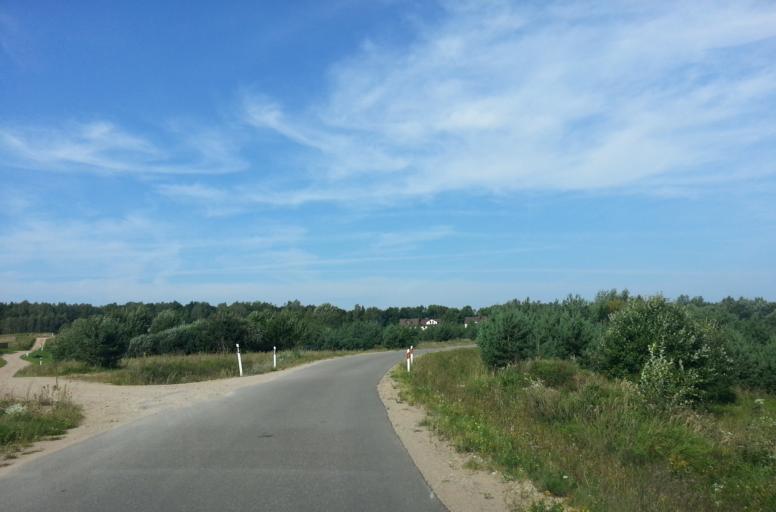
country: LT
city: Grigiskes
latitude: 54.7256
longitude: 25.0741
